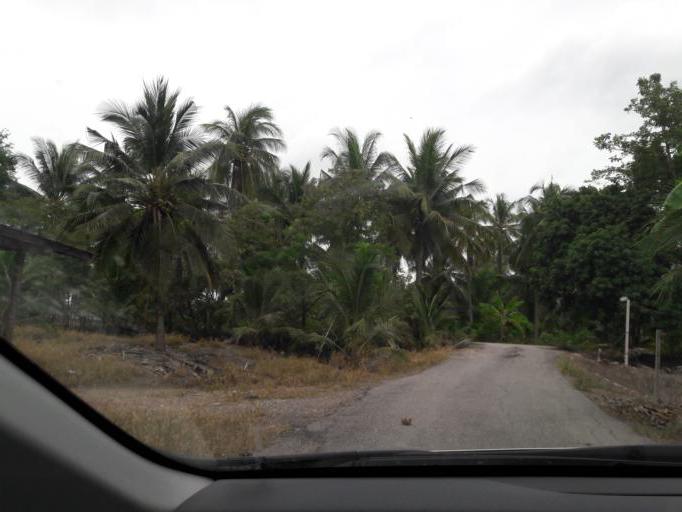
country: TH
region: Samut Sakhon
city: Ban Phaeo
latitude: 13.6001
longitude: 100.0272
